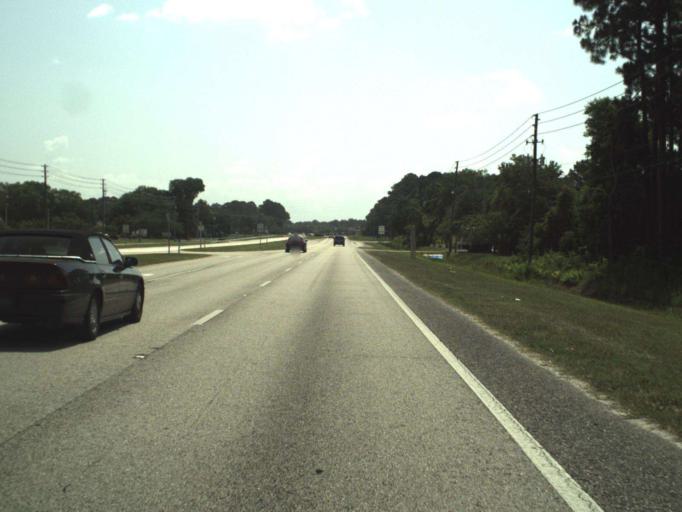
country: US
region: Florida
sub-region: Volusia County
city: North DeLand
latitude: 29.0549
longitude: -81.2927
